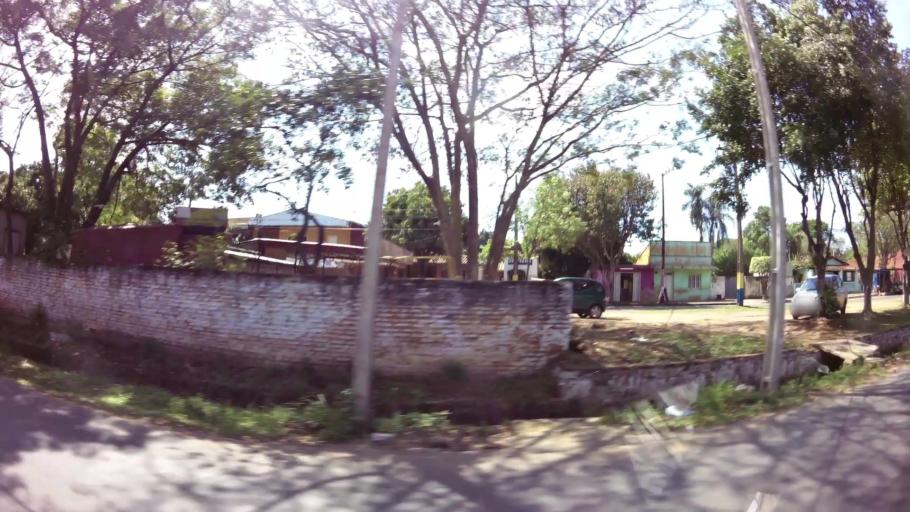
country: PY
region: Central
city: San Lorenzo
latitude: -25.2733
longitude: -57.4962
